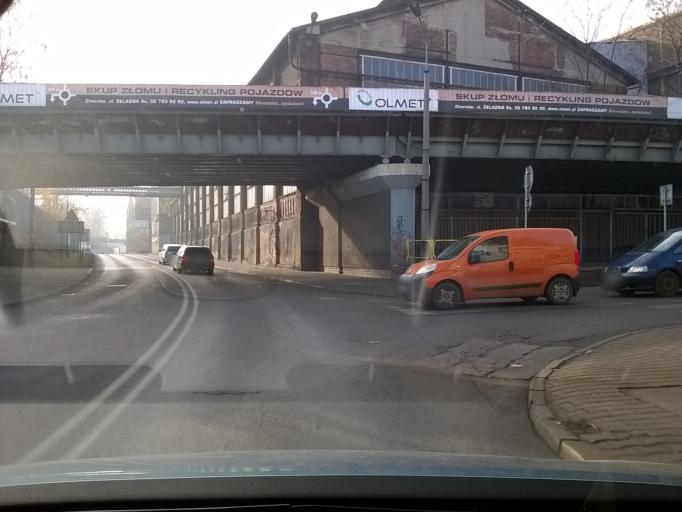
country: PL
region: Silesian Voivodeship
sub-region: Swietochlowice
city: Swietochlowice
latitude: 50.2788
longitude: 18.9431
